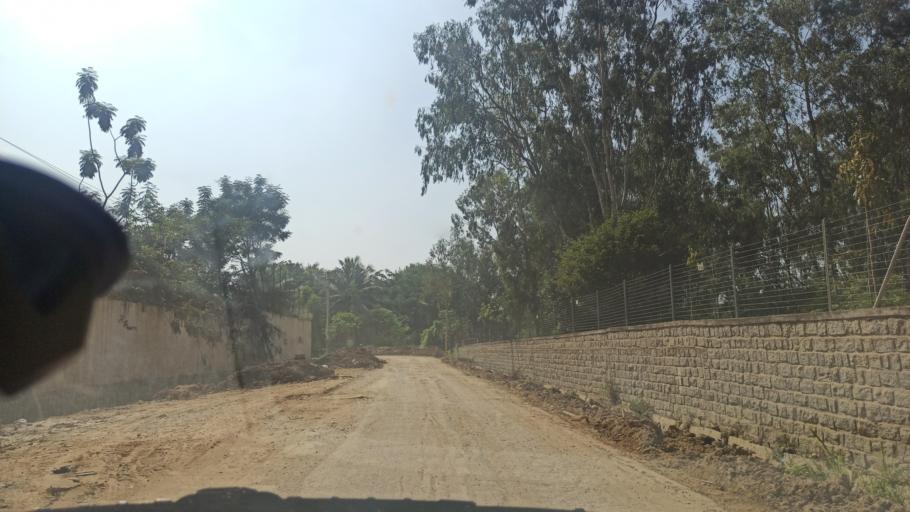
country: IN
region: Karnataka
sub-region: Bangalore Urban
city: Bangalore
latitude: 12.9162
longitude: 77.6891
